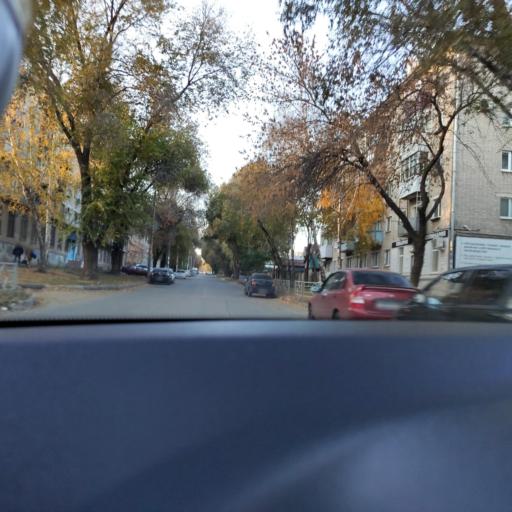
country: RU
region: Samara
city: Samara
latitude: 53.2114
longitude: 50.2357
